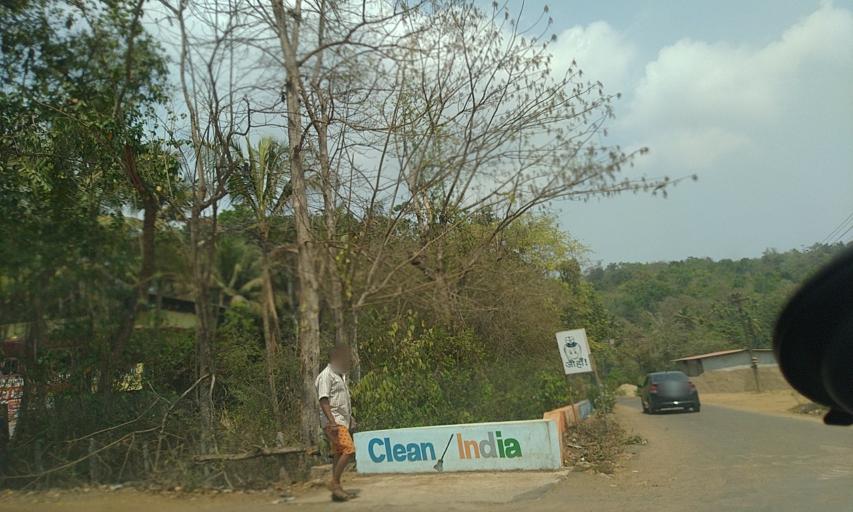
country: IN
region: Goa
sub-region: North Goa
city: Pernem
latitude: 15.7135
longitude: 73.7986
